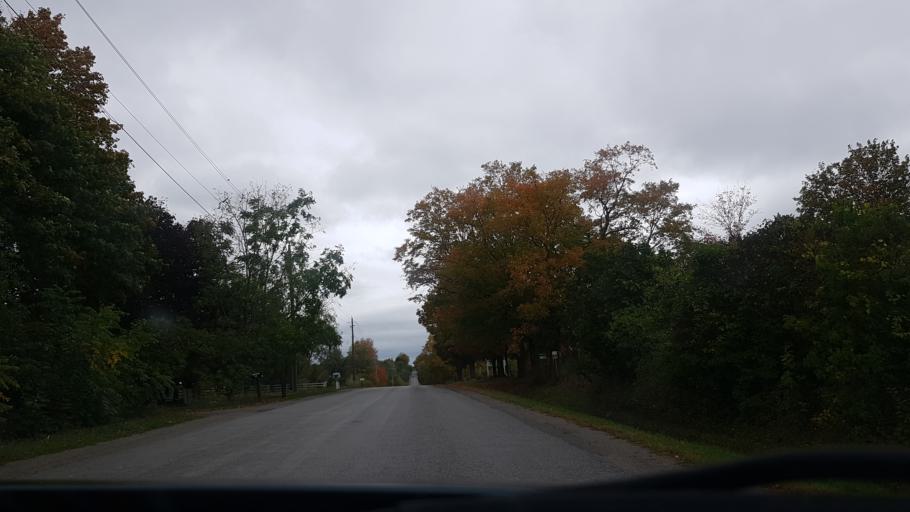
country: CA
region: Ontario
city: Peterborough
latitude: 44.2524
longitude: -78.4141
